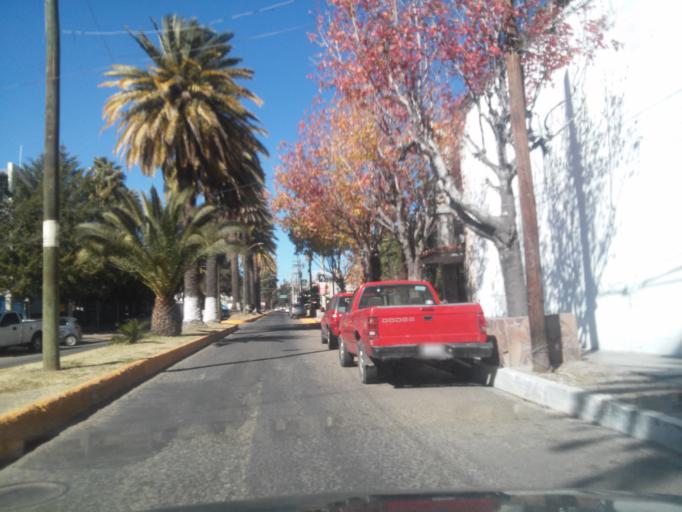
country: MX
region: Durango
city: Victoria de Durango
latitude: 24.0230
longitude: -104.6785
